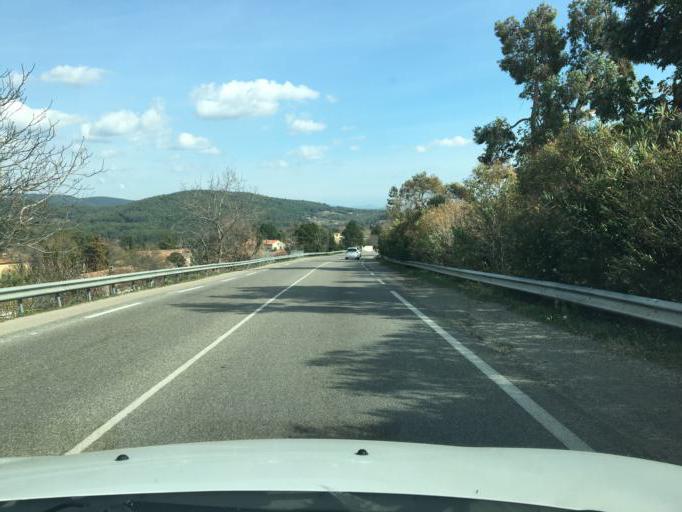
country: FR
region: Provence-Alpes-Cote d'Azur
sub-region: Departement du Var
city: Flayosc
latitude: 43.5357
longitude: 6.3921
